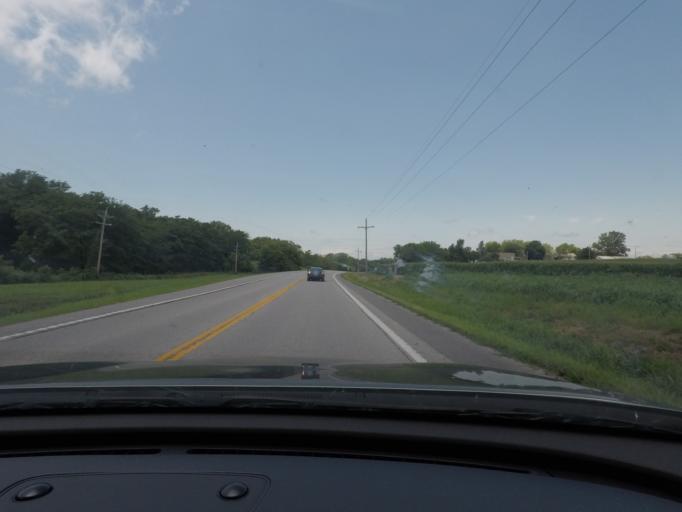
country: US
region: Missouri
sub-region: Saline County
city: Marshall
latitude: 39.1740
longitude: -93.2991
